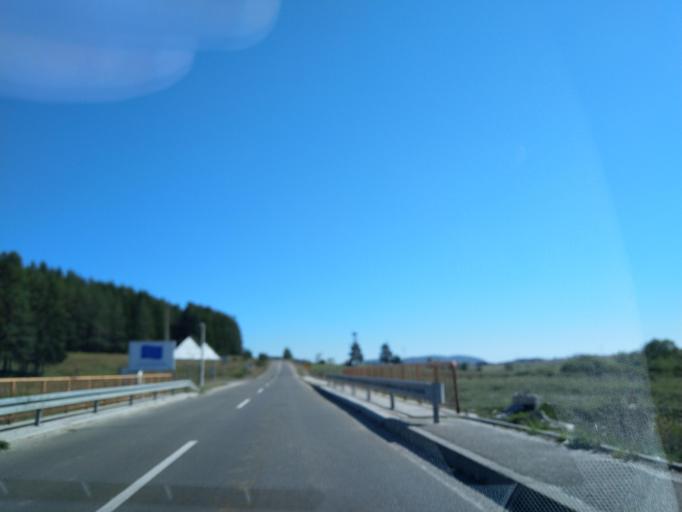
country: RS
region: Central Serbia
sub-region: Zlatiborski Okrug
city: Sjenica
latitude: 43.2695
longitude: 20.0244
